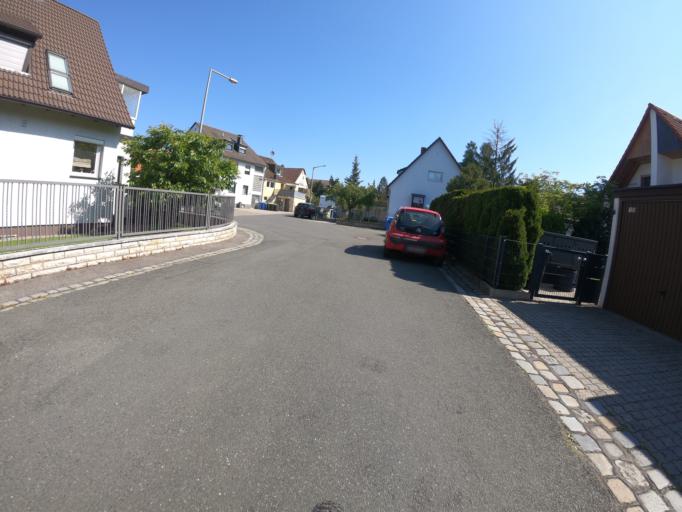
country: DE
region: Bavaria
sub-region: Regierungsbezirk Mittelfranken
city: Stein
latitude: 49.4078
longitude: 11.0257
